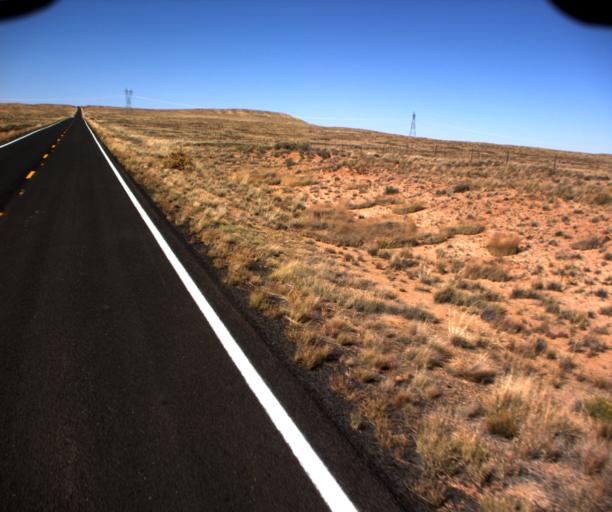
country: US
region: Arizona
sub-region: Coconino County
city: Tuba City
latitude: 35.9465
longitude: -110.9160
